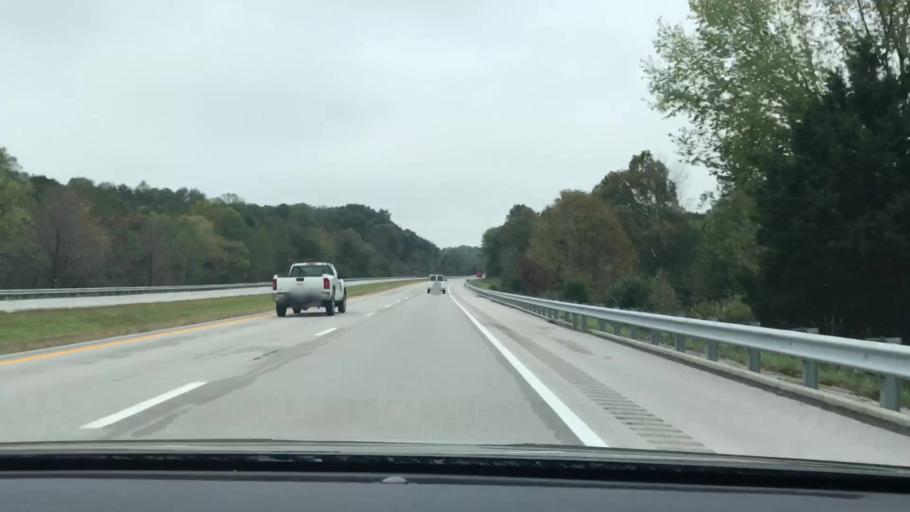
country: US
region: Kentucky
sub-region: Pulaski County
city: Somerset
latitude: 37.0979
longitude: -84.8351
